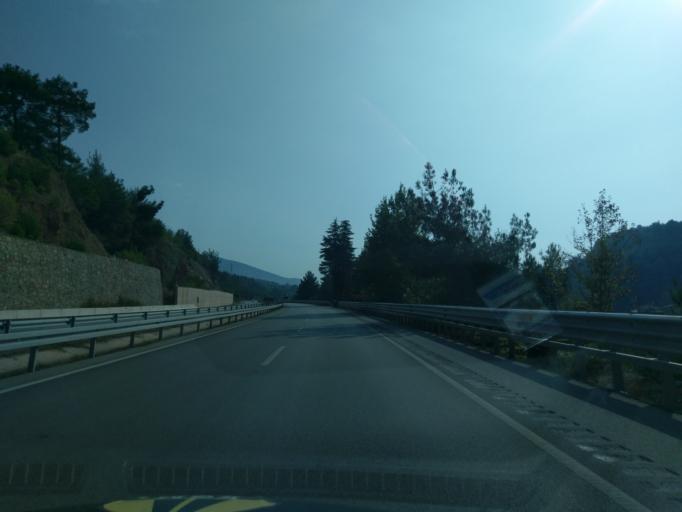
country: TR
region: Amasya
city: Tekke
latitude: 40.7448
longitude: 36.1059
